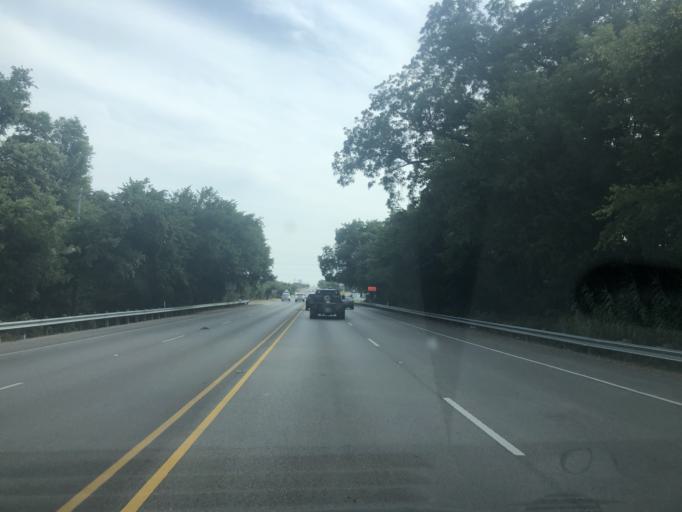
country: US
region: Texas
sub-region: Tarrant County
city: Benbrook
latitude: 32.6956
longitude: -97.4549
